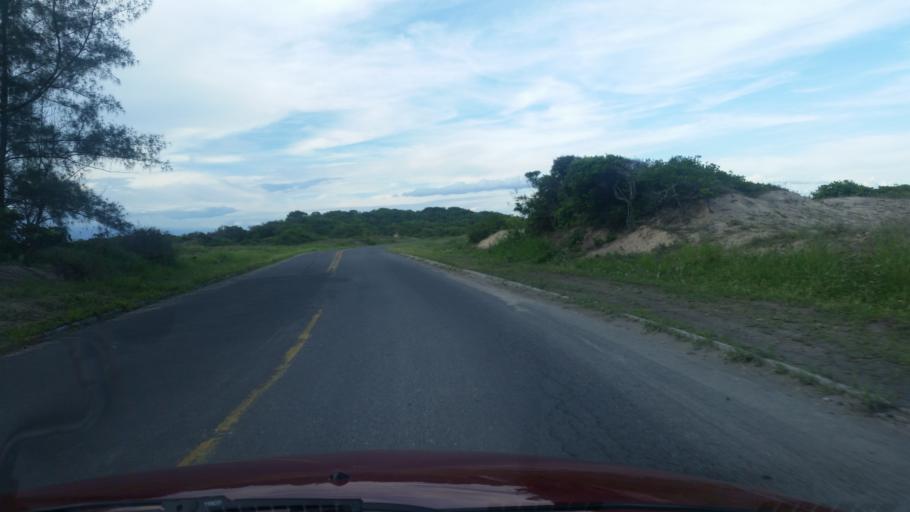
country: BR
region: Sao Paulo
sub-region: Iguape
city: Iguape
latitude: -24.7977
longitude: -47.6255
